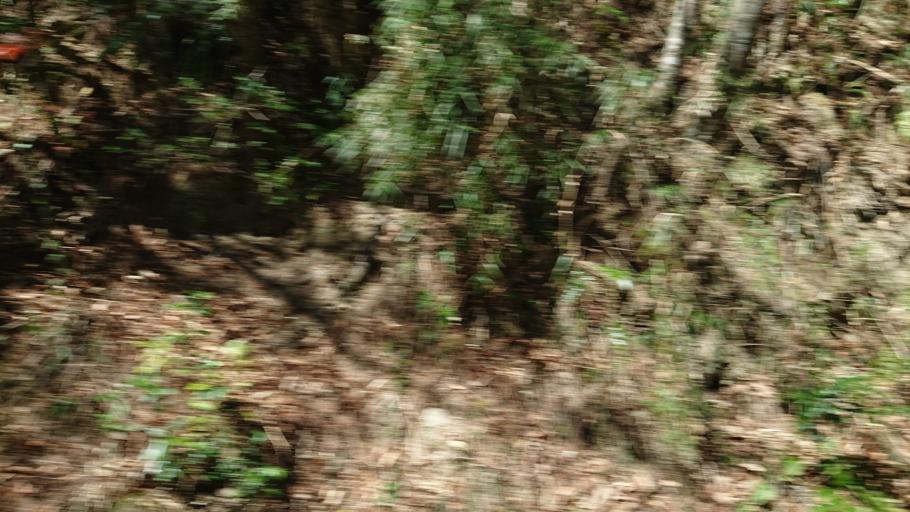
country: TW
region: Taiwan
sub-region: Hualien
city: Hualian
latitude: 24.3488
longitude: 121.3078
